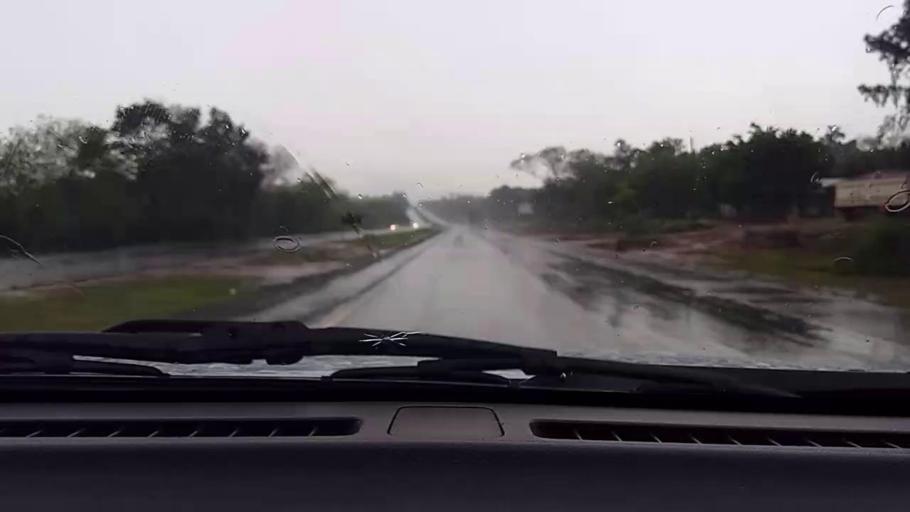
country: PY
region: Caaguazu
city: Repatriacion
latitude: -25.4471
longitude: -55.8903
